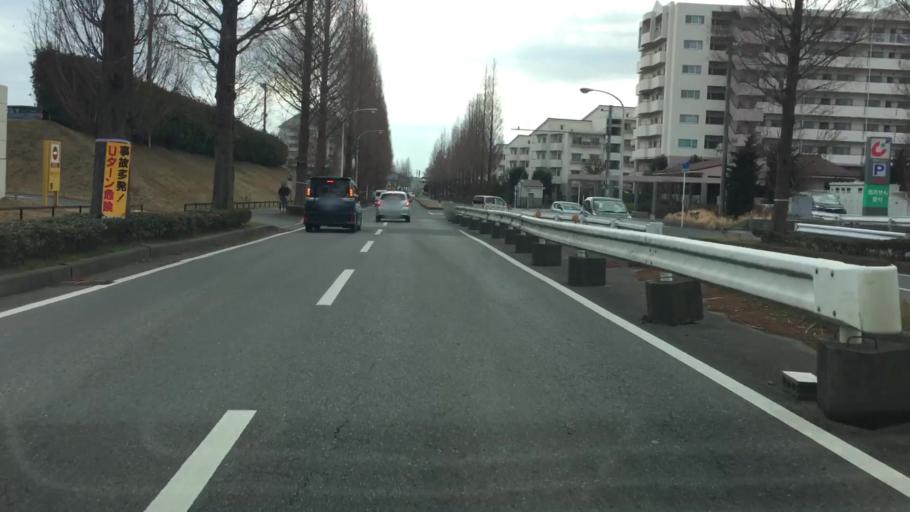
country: JP
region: Chiba
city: Shiroi
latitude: 35.8040
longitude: 140.1599
